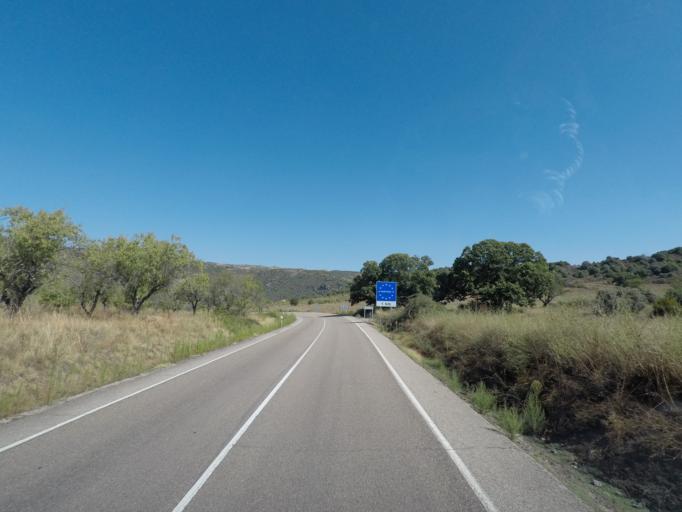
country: ES
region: Castille and Leon
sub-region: Provincia de Salamanca
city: Villarino de los Aires
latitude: 41.2951
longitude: -6.4692
